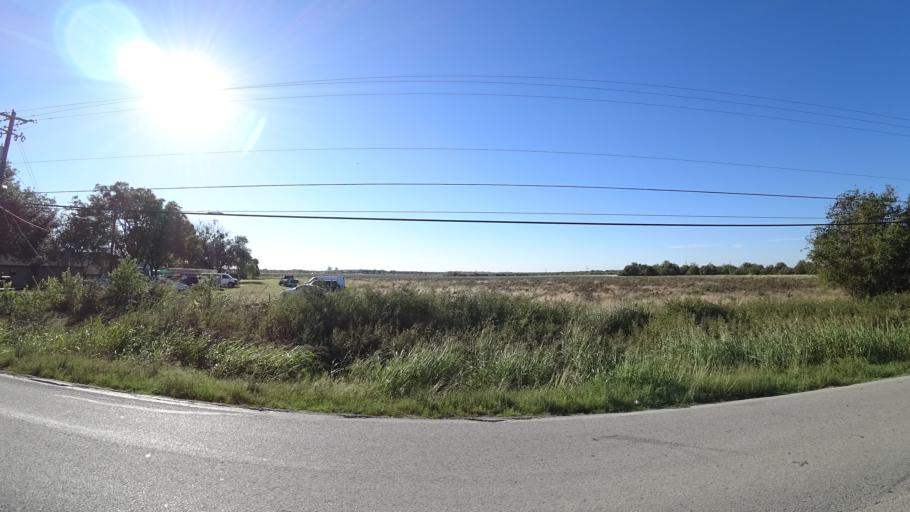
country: US
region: Texas
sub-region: Travis County
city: Manor
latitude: 30.3272
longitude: -97.6355
